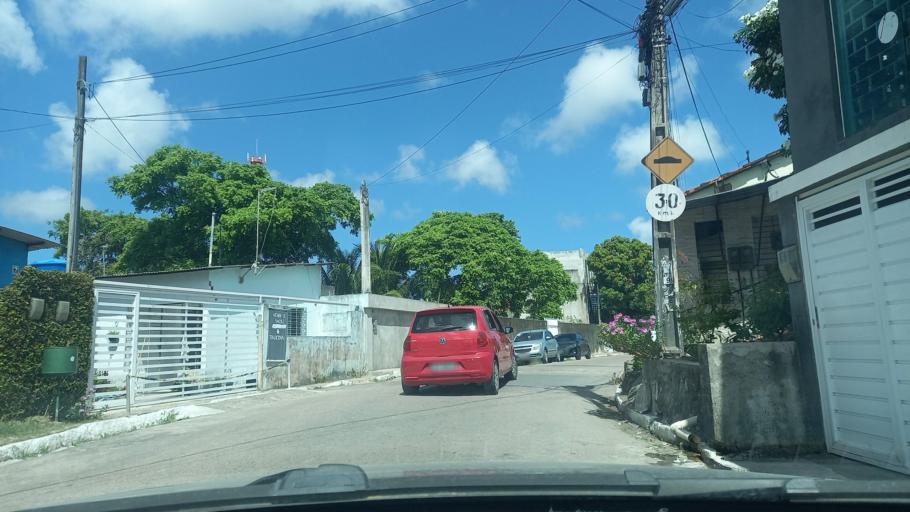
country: BR
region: Pernambuco
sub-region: Paulista
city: Paulista
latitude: -7.9398
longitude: -34.8754
